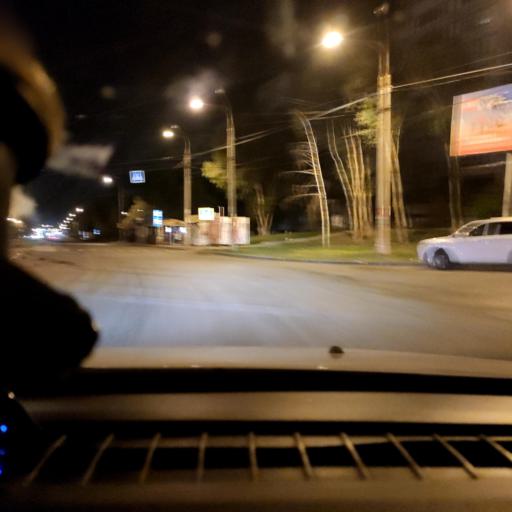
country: RU
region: Samara
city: Samara
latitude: 53.2171
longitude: 50.2219
